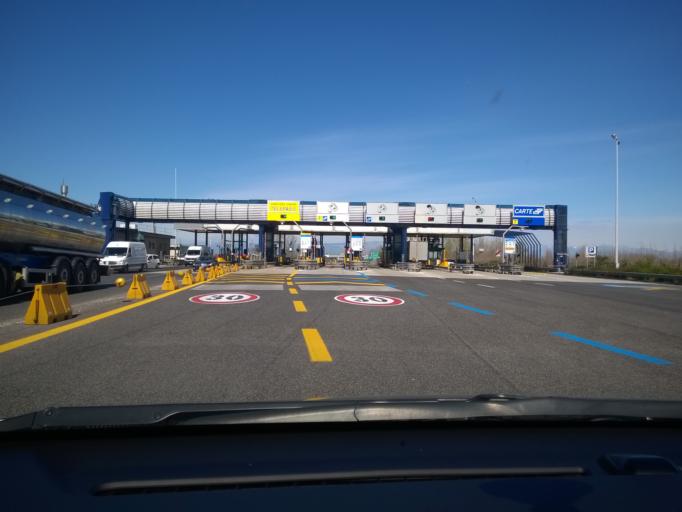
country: IT
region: Veneto
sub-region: Provincia di Venezia
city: Portogruaro
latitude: 45.7980
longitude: 12.8253
